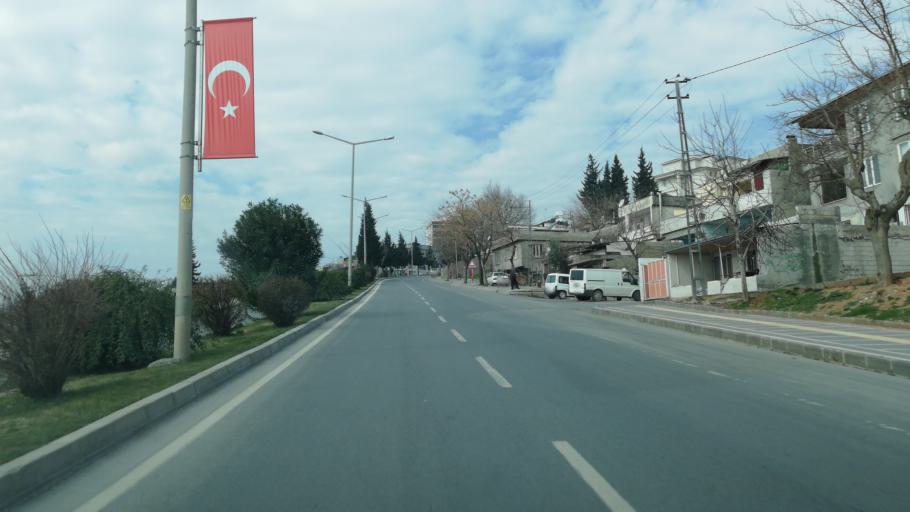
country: TR
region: Kahramanmaras
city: Kahramanmaras
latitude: 37.5722
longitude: 36.9117
